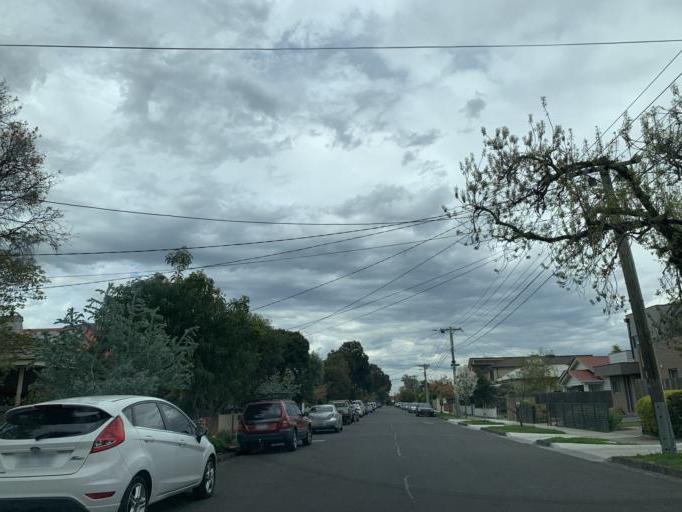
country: AU
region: Victoria
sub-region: Moreland
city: Coburg
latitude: -37.7526
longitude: 144.9678
